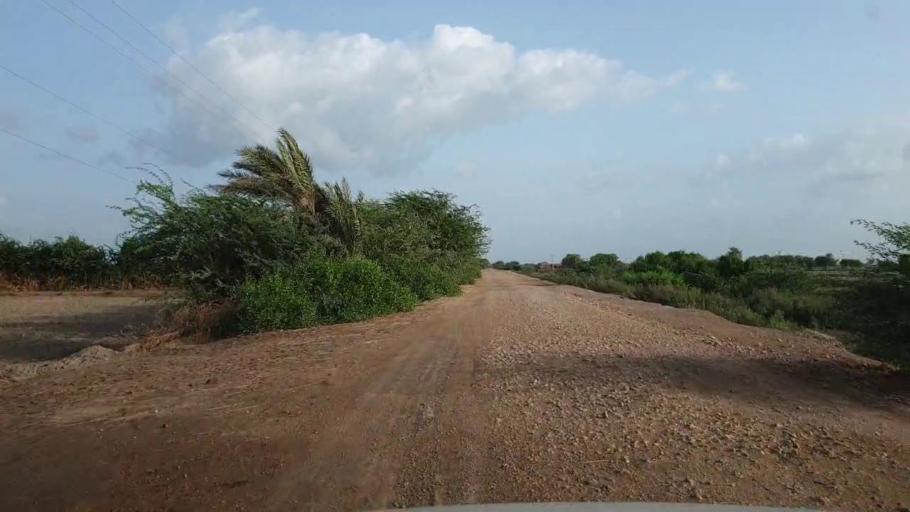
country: PK
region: Sindh
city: Kario
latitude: 24.8112
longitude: 68.6470
